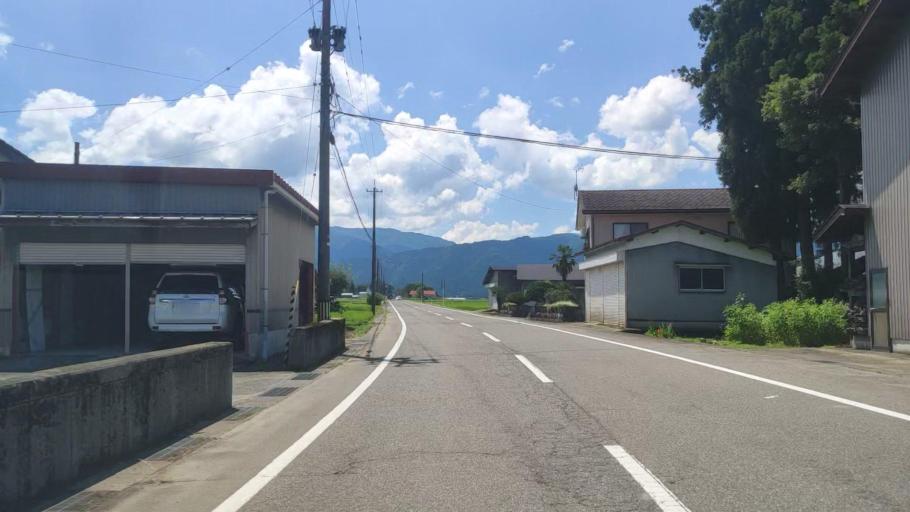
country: JP
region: Fukui
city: Ono
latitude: 35.9684
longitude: 136.5278
